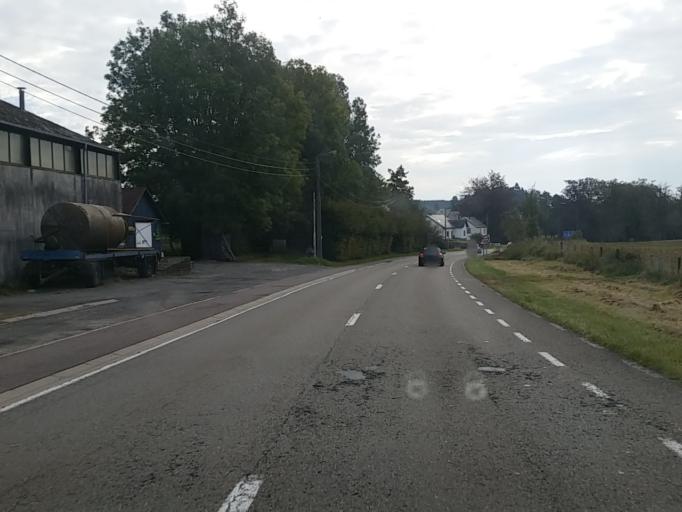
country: BE
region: Wallonia
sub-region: Province du Luxembourg
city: Tintigny
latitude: 49.6851
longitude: 5.5051
